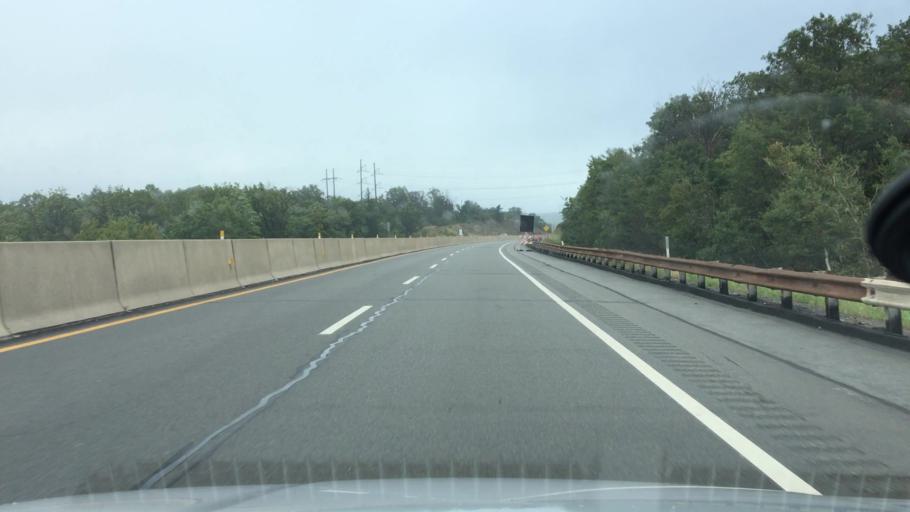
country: US
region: Pennsylvania
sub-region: Luzerne County
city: Hudson
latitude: 41.2248
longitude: -75.7974
